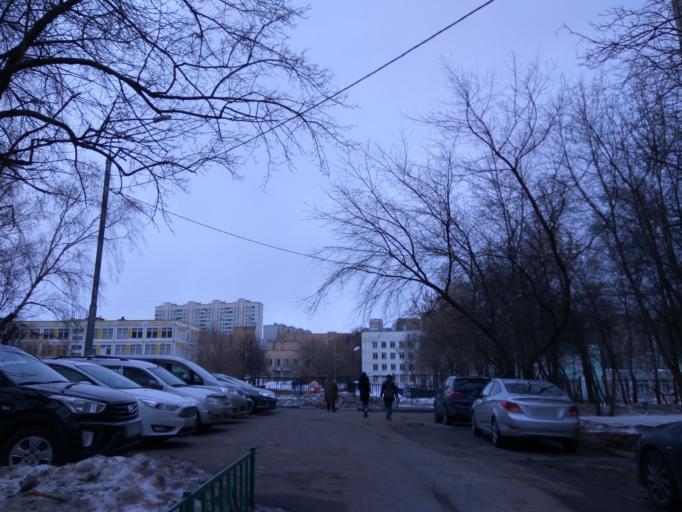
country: RU
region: Moscow
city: Biryulevo
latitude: 55.5920
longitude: 37.6686
